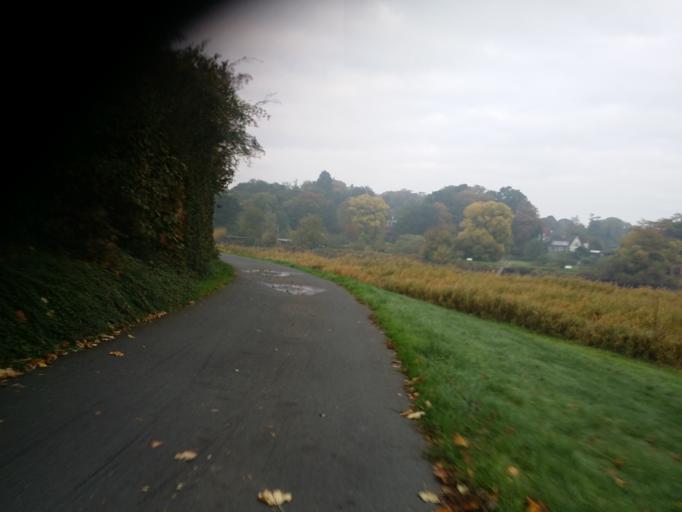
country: DE
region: Lower Saxony
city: Ritterhude
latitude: 53.1626
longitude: 8.6902
